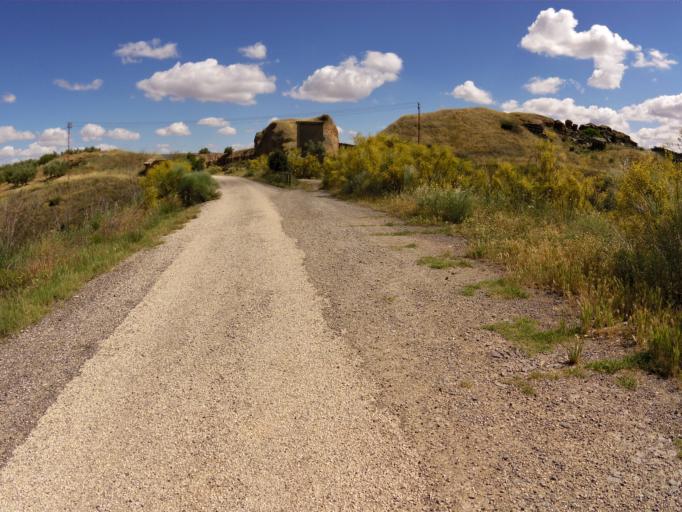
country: ES
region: Andalusia
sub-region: Provincia de Jaen
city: Alcaudete
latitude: 37.6331
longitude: -4.0827
